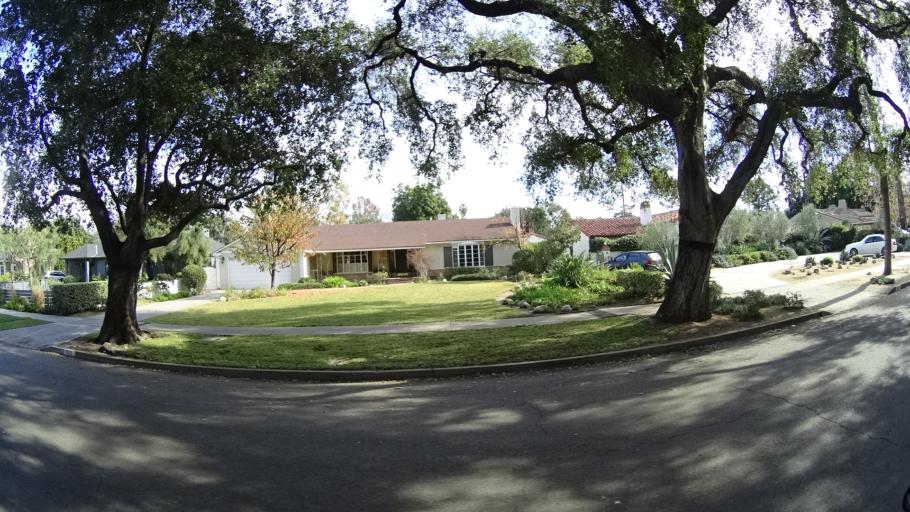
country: US
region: California
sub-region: Orange County
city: Santa Ana
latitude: 33.7632
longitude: -117.8751
